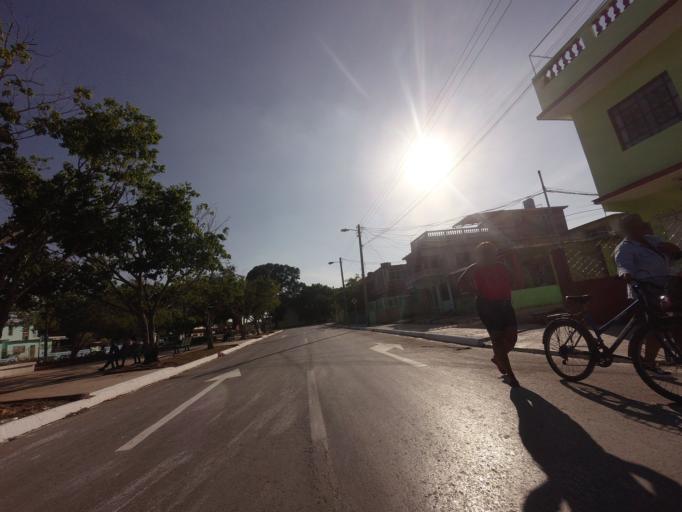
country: CU
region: Ciego de Avila
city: Ciego de Avila
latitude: 21.8443
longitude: -78.7714
